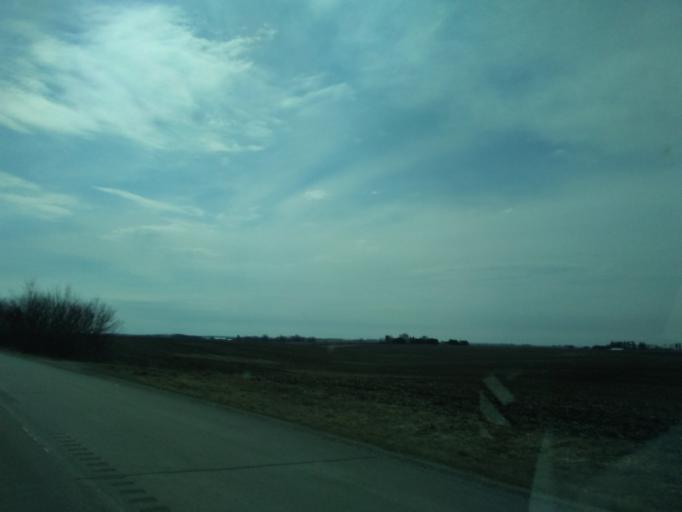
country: US
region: Minnesota
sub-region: Fillmore County
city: Harmony
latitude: 43.5075
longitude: -91.8711
